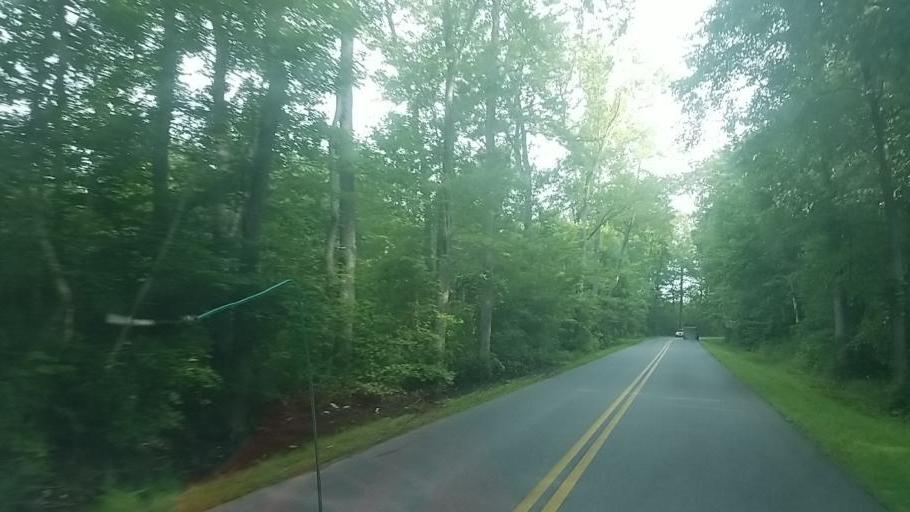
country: US
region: Maryland
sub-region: Worcester County
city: West Ocean City
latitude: 38.3291
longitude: -75.1553
